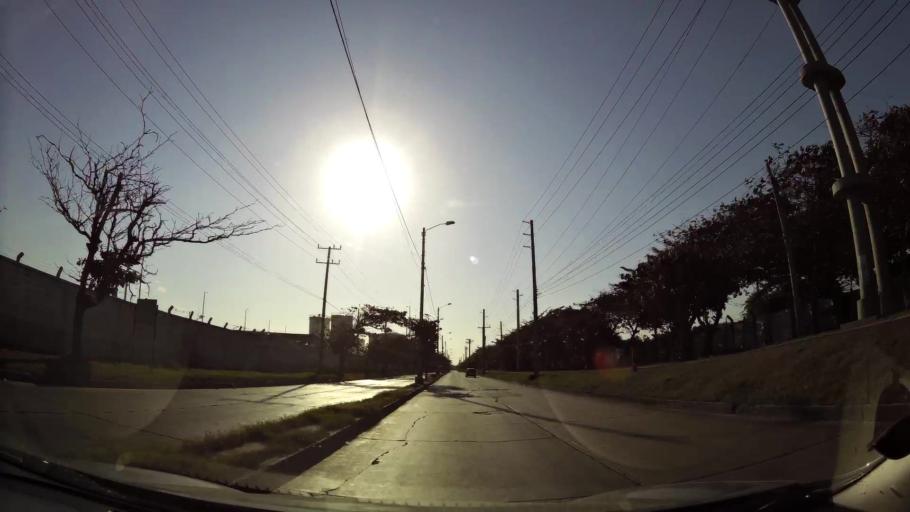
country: CO
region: Atlantico
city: Barranquilla
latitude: 11.0353
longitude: -74.8141
